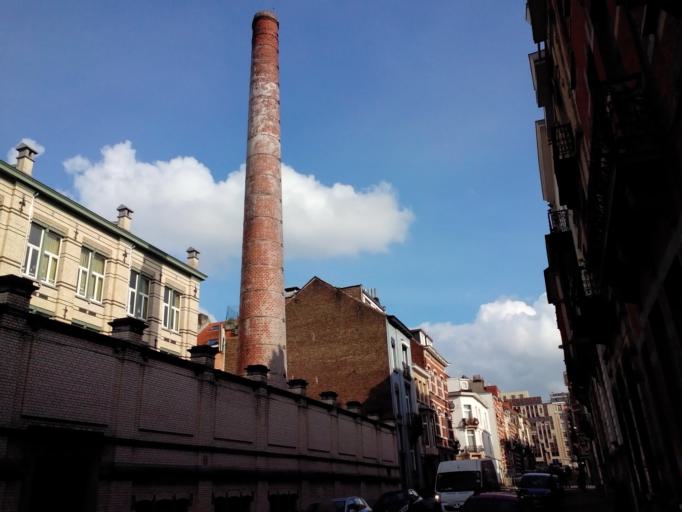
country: BE
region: Brussels Capital
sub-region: Bruxelles-Capitale
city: Brussels
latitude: 50.8459
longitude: 4.3865
